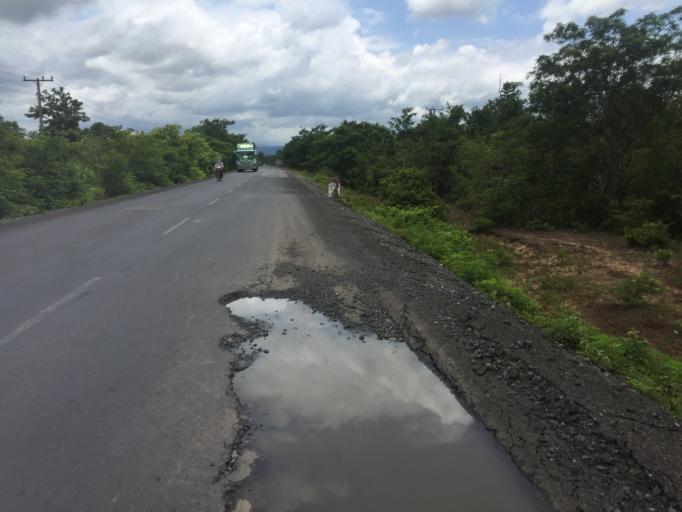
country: LA
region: Salavan
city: Salavan
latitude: 15.8389
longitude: 106.3879
